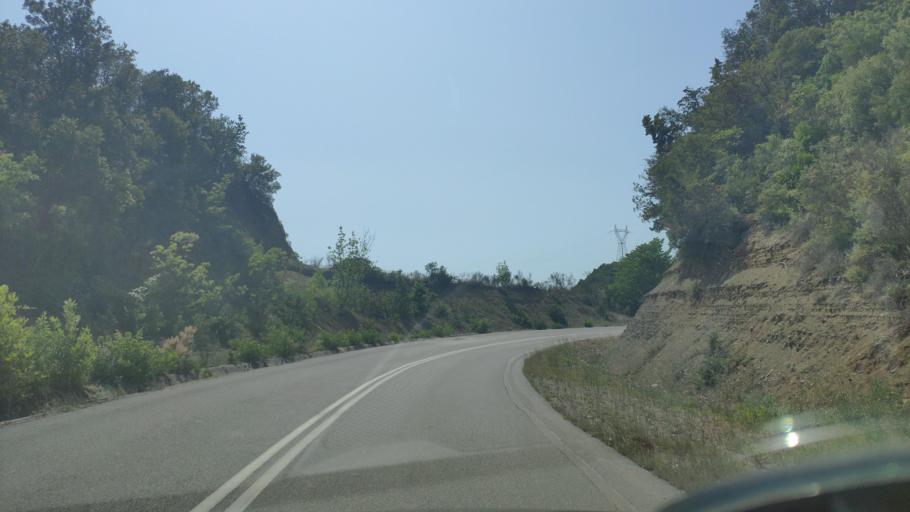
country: GR
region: Epirus
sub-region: Nomos Artas
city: Ano Kalentini
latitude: 39.2196
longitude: 21.1381
